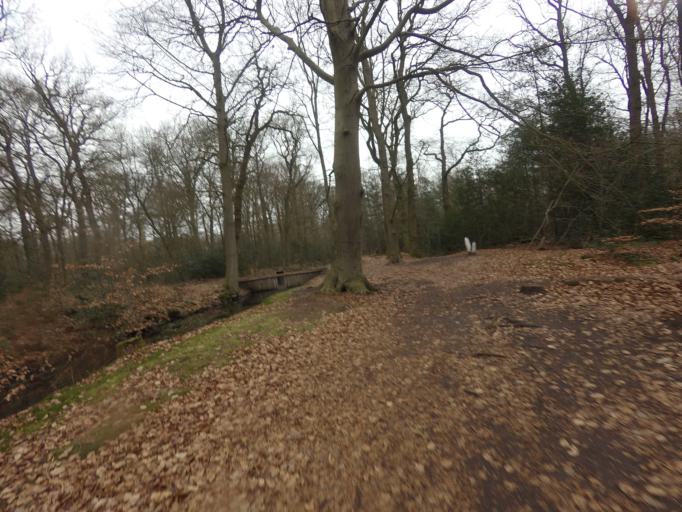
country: NL
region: Friesland
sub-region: Gemeente Gaasterlan-Sleat
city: Oudemirdum
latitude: 52.8607
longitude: 5.4970
